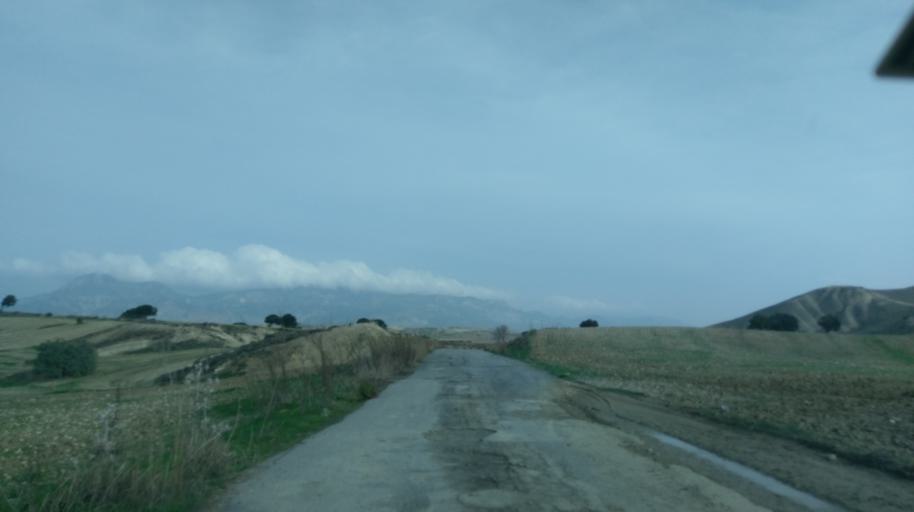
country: CY
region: Lefkosia
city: Morfou
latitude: 35.2580
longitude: 33.0879
